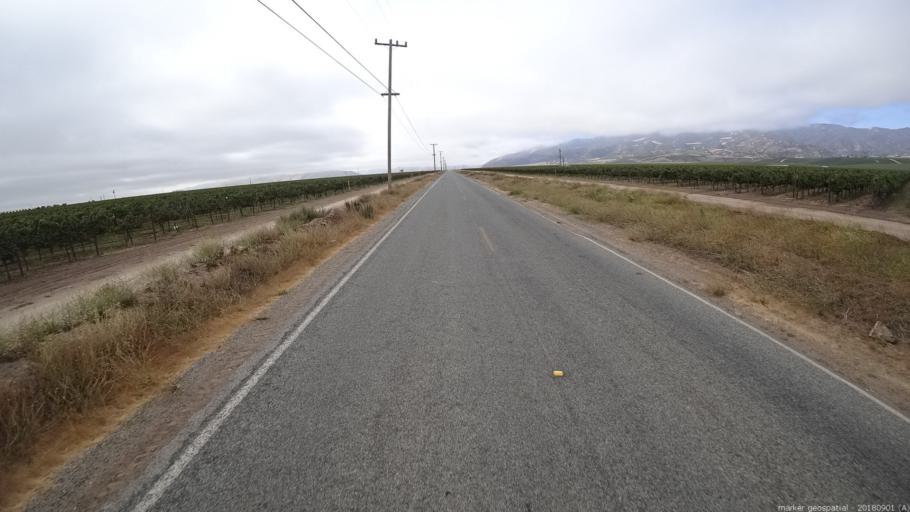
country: US
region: California
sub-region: Monterey County
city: Soledad
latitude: 36.3552
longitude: -121.3206
